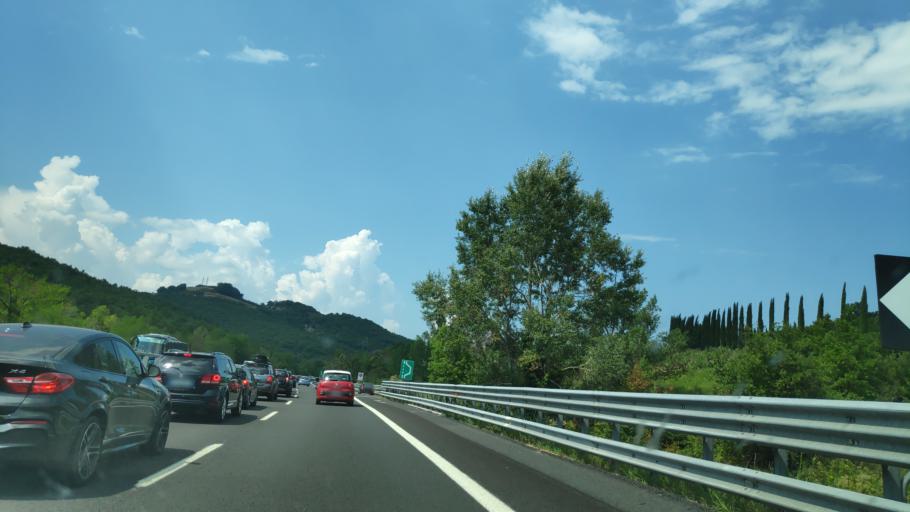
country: IT
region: Umbria
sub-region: Provincia di Terni
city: Stazione di Allerona
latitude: 42.8045
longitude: 12.0416
